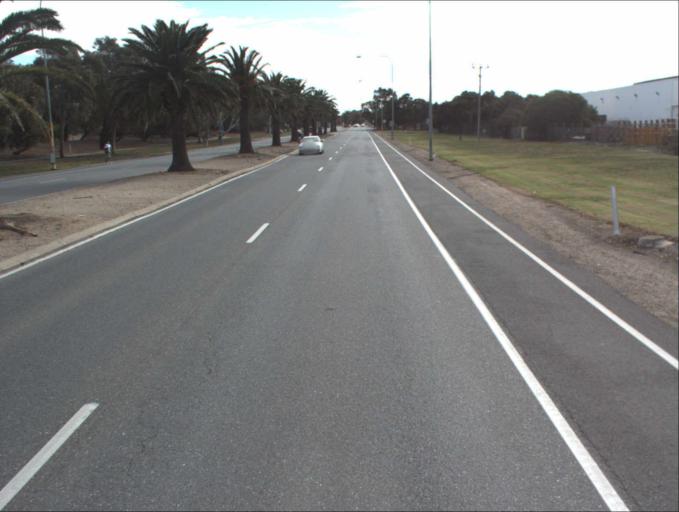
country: AU
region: South Australia
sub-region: Charles Sturt
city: West Lakes Shore
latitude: -34.8579
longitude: 138.5026
